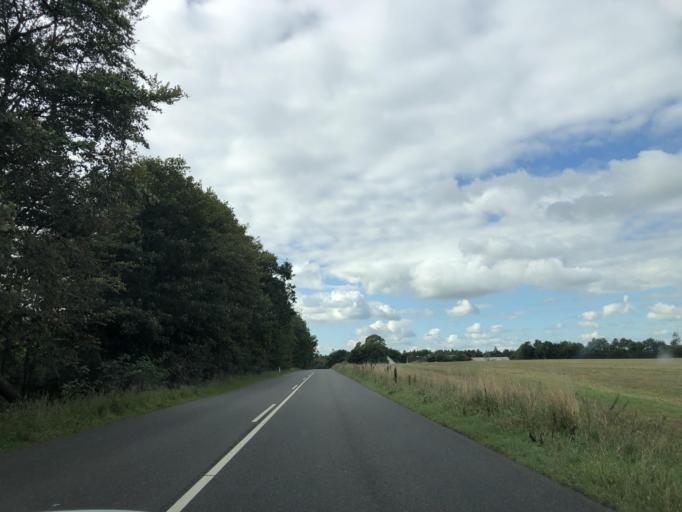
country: DK
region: North Denmark
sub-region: Rebild Kommune
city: Stovring
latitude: 56.8697
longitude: 9.7192
